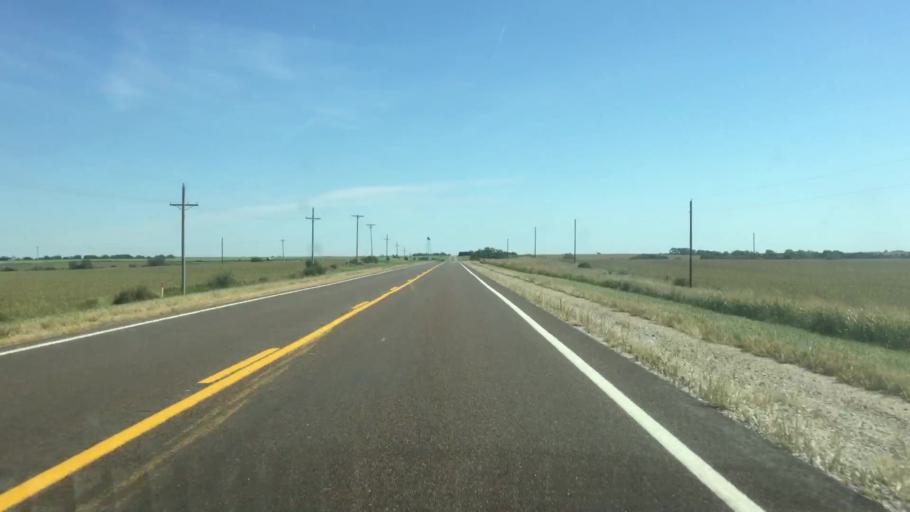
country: US
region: Nebraska
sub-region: Jefferson County
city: Fairbury
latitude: 40.1472
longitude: -97.3346
